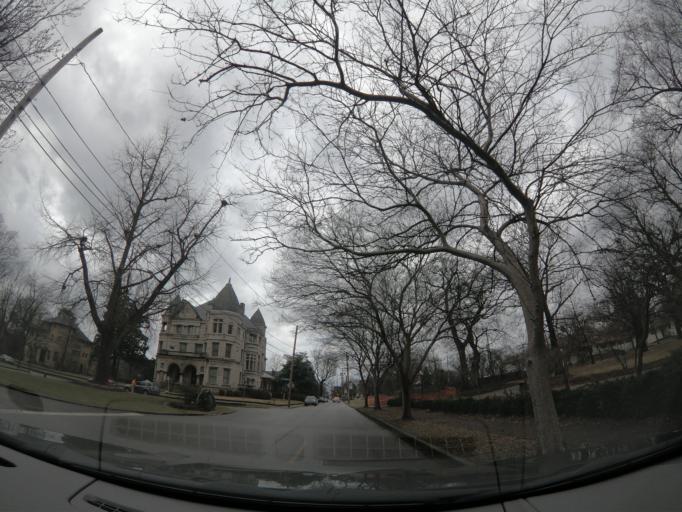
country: US
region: Kentucky
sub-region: Jefferson County
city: Louisville
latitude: 38.2293
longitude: -85.7628
